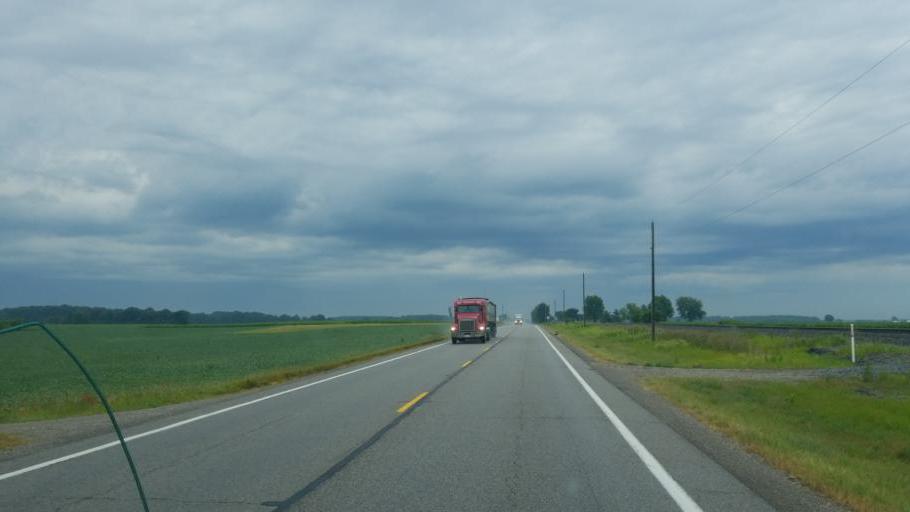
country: US
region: Ohio
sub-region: Williams County
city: Edgerton
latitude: 41.4398
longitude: -84.7971
